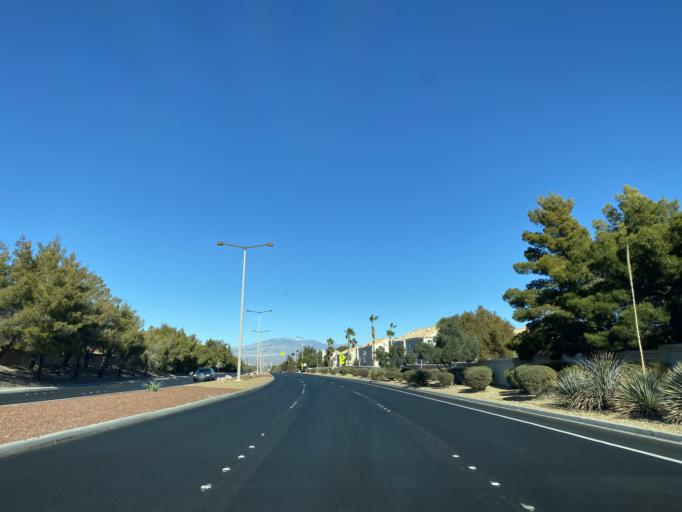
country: US
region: Nevada
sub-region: Clark County
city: Summerlin South
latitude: 36.2042
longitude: -115.2790
